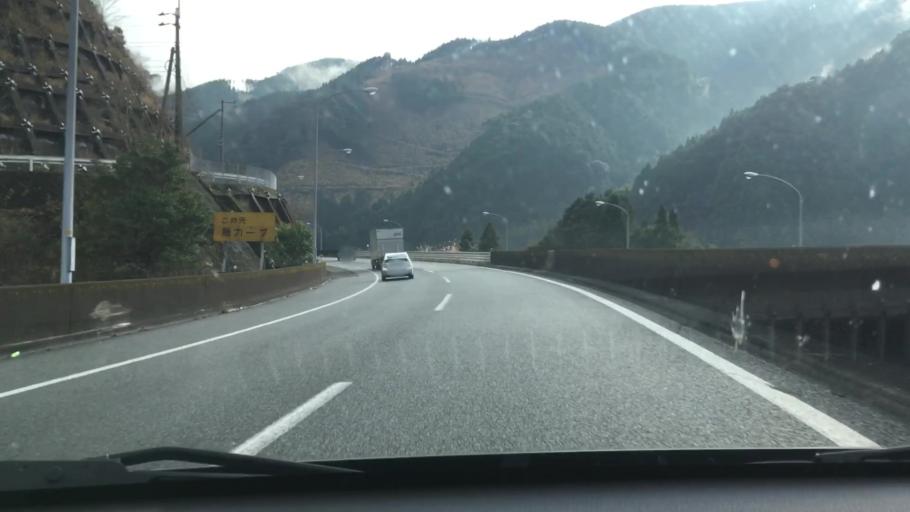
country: JP
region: Kumamoto
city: Yatsushiro
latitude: 32.4039
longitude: 130.6976
